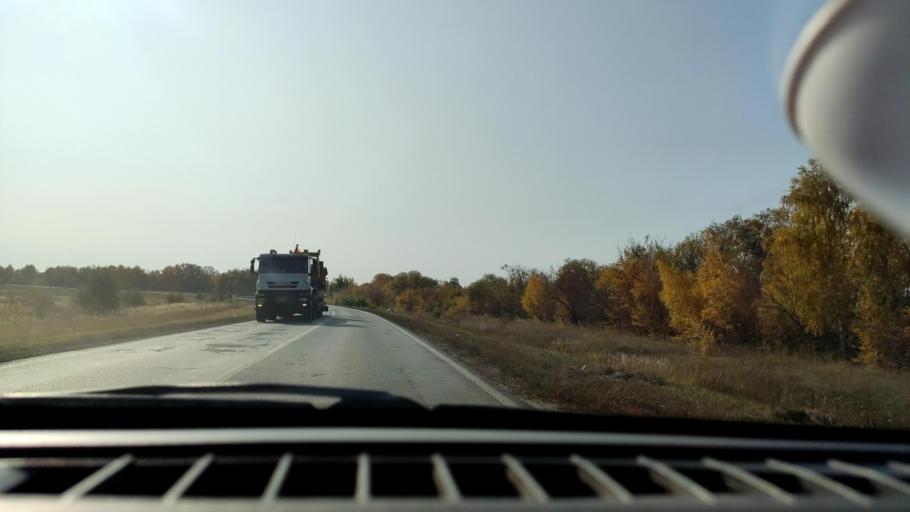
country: RU
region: Samara
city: Smyshlyayevka
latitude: 53.1385
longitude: 50.3771
